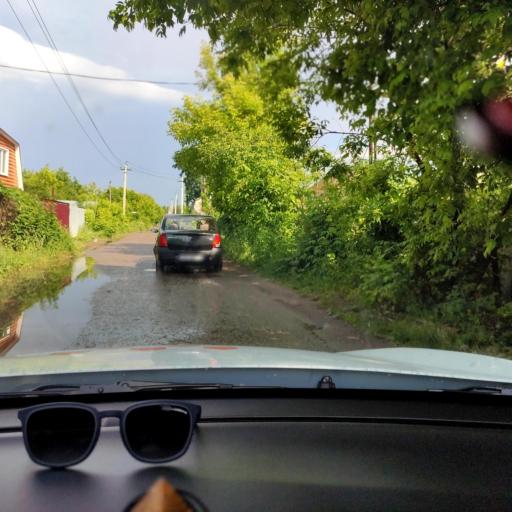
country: RU
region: Tatarstan
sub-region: Zelenodol'skiy Rayon
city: Vasil'yevo
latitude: 55.8279
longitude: 48.7539
